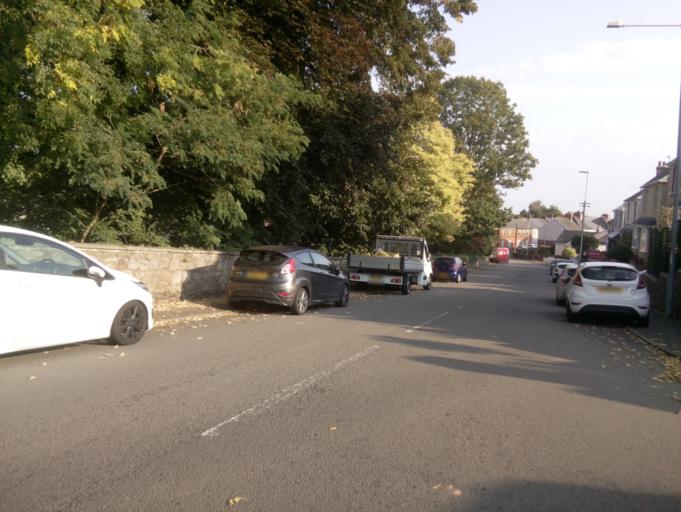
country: GB
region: Wales
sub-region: Torfaen County Borough
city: Pontypool
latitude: 51.6906
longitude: -3.0284
